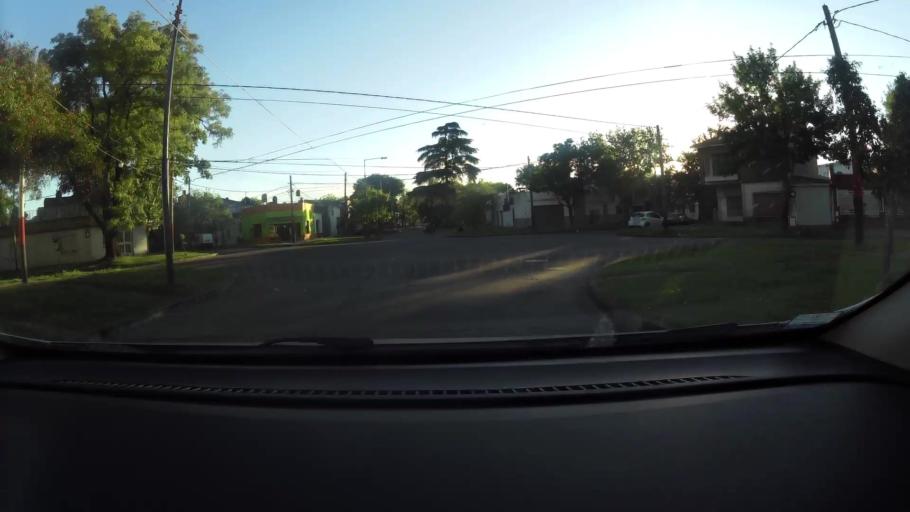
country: AR
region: Santa Fe
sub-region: Departamento de Rosario
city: Rosario
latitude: -32.9688
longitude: -60.6695
